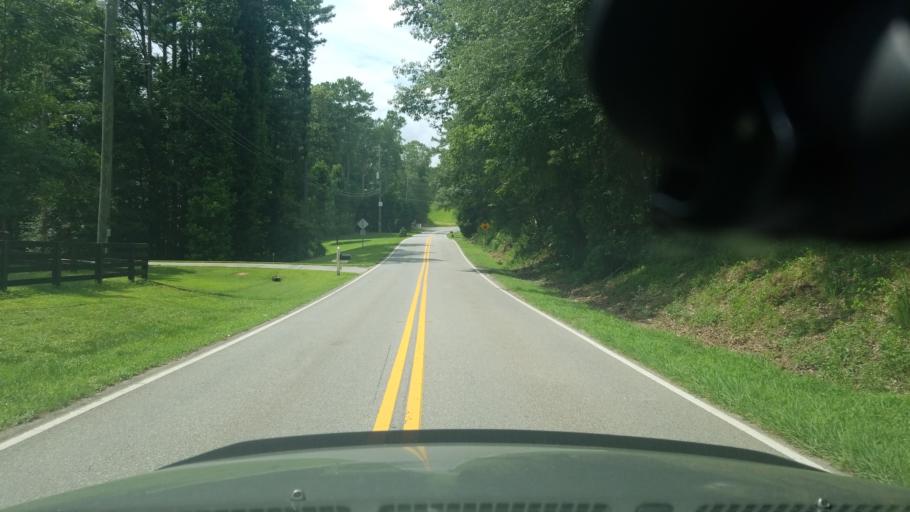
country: US
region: Georgia
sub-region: Forsyth County
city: Cumming
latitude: 34.2959
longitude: -84.2389
